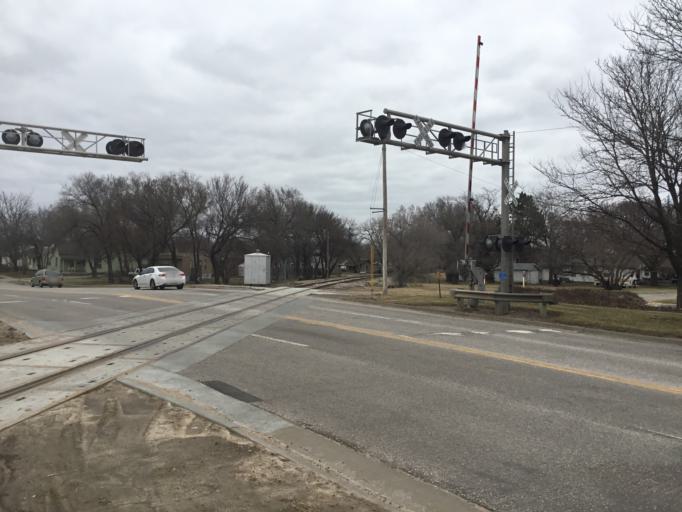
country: US
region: Kansas
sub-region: Sedgwick County
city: Wichita
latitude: 37.6775
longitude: -97.3713
